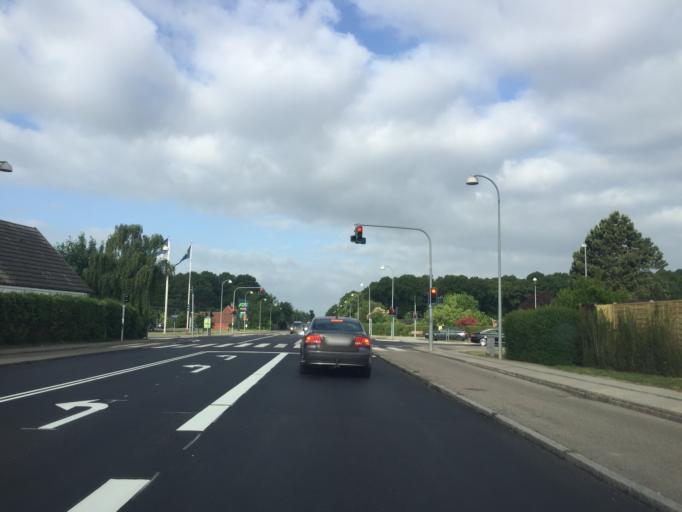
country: DK
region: Capital Region
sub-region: Brondby Kommune
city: Brondbyvester
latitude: 55.6547
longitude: 12.4295
